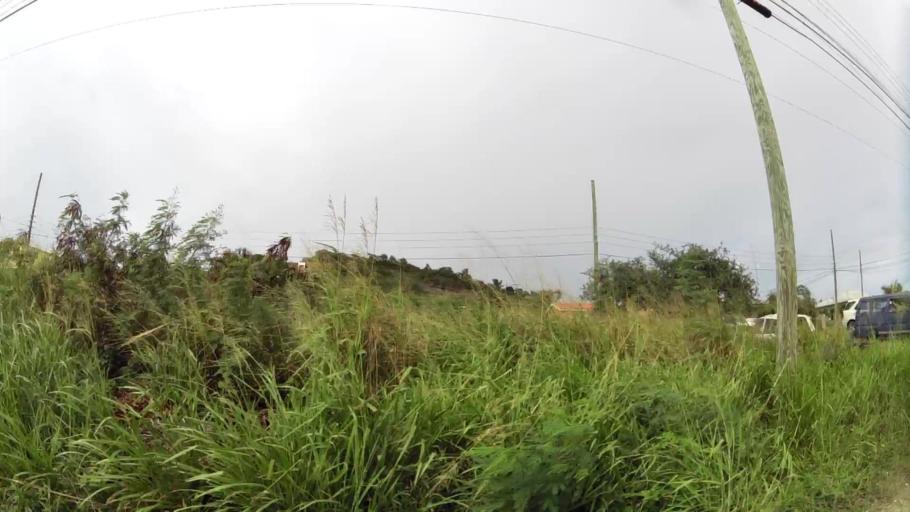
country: AG
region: Saint John
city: Potters Village
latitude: 17.0968
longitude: -61.8157
